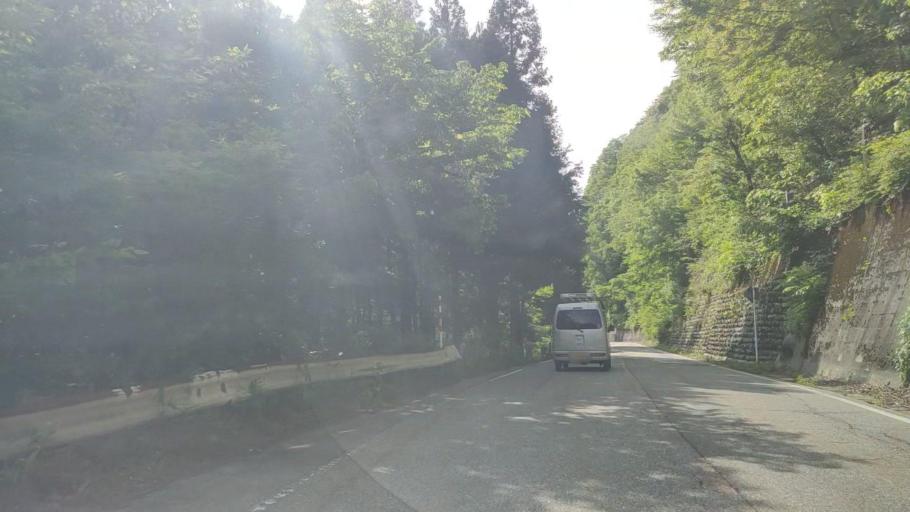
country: JP
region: Gifu
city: Takayama
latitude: 36.2702
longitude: 137.3956
